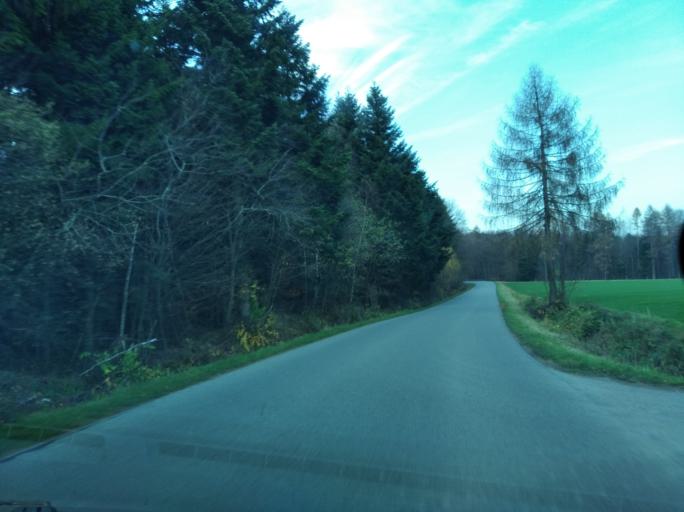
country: PL
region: Subcarpathian Voivodeship
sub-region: Powiat ropczycko-sedziszowski
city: Zagorzyce
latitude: 49.9569
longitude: 21.6936
